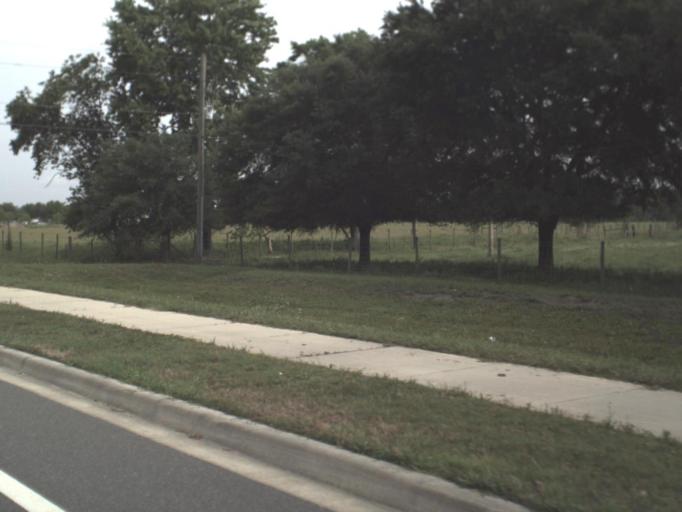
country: US
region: Florida
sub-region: Clay County
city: Green Cove Springs
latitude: 29.9703
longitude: -81.5020
